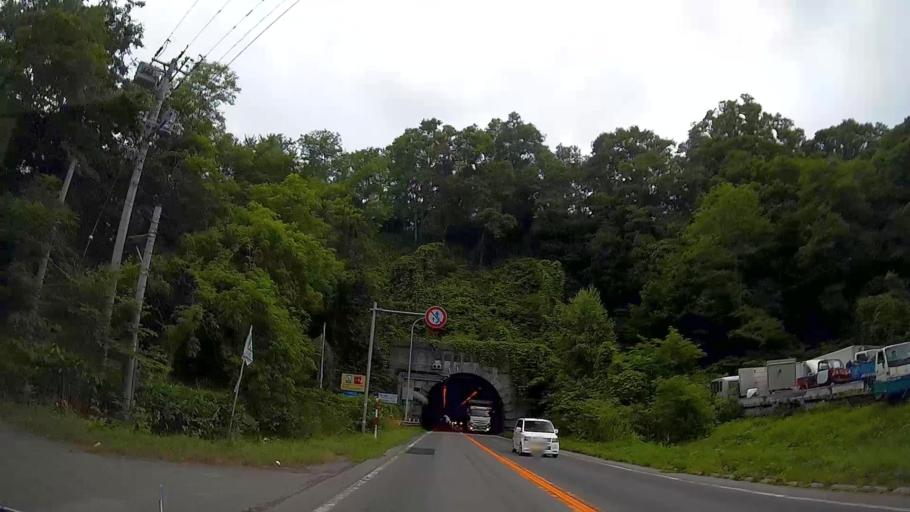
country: JP
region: Hokkaido
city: Nanae
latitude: 42.1190
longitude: 140.5346
